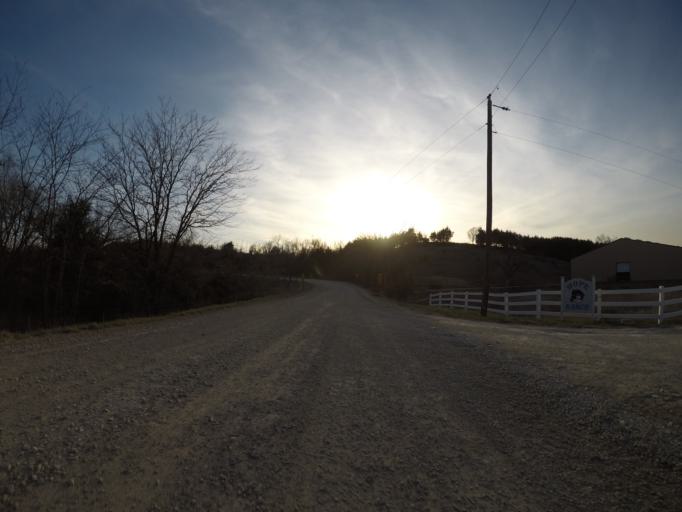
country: US
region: Kansas
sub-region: Riley County
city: Ogden
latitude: 39.2327
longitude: -96.6991
